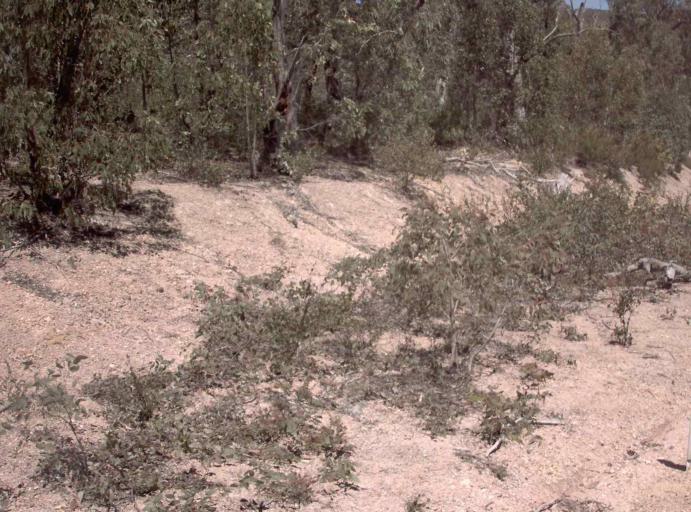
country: AU
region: New South Wales
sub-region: Snowy River
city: Jindabyne
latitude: -37.1190
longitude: 148.2420
